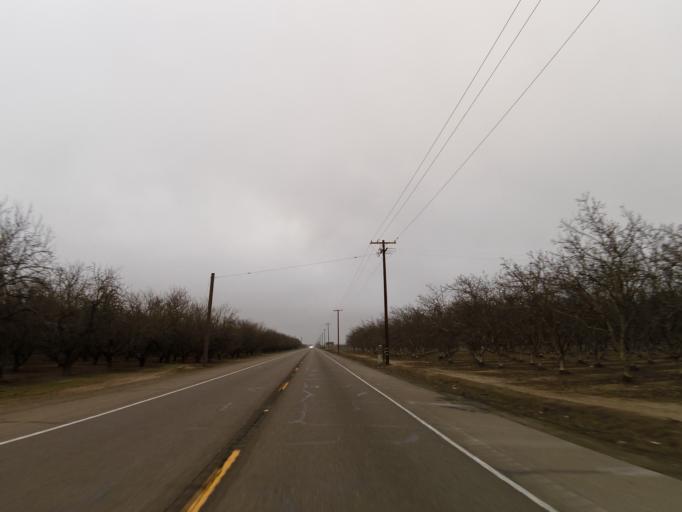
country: US
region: California
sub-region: Stanislaus County
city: Riverdale Park
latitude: 37.6381
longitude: -121.0895
